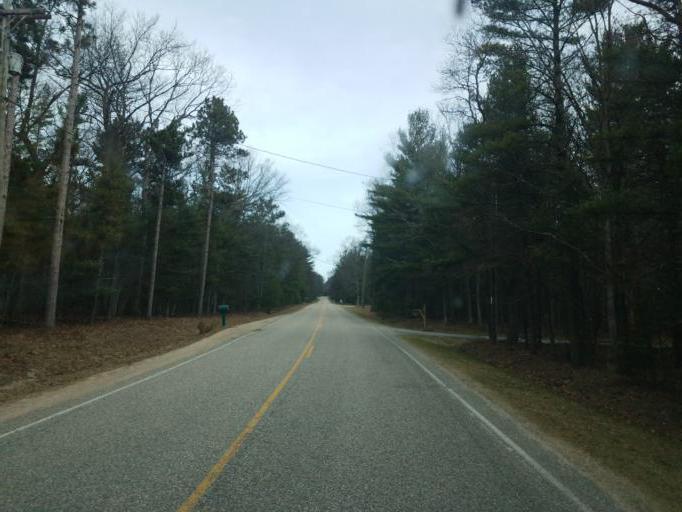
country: US
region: Michigan
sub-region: Oceana County
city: Hart
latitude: 43.7617
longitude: -86.4417
